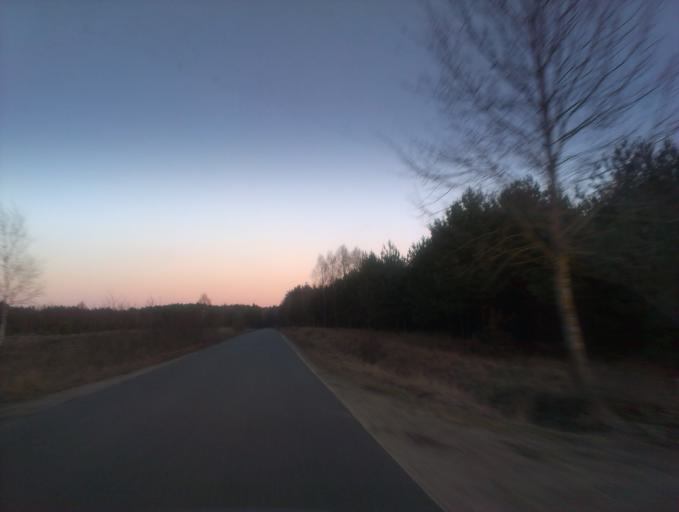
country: PL
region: Greater Poland Voivodeship
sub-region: Powiat zlotowski
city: Okonek
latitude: 53.5348
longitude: 16.8833
